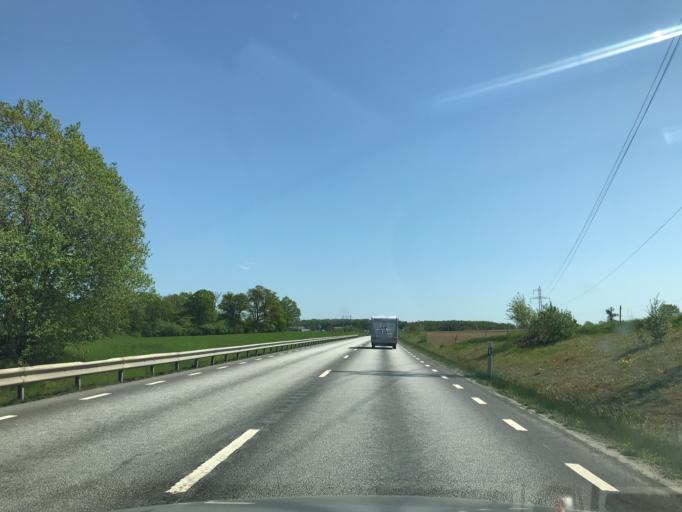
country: SE
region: Skane
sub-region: Klippans Kommun
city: Klippan
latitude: 56.1173
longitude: 13.1344
